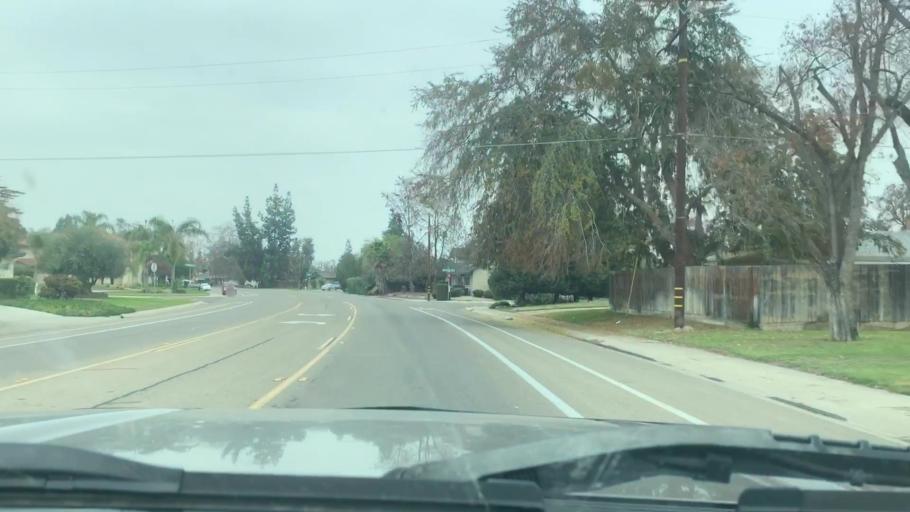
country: US
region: California
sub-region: Tulare County
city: Visalia
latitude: 36.3141
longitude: -119.3230
